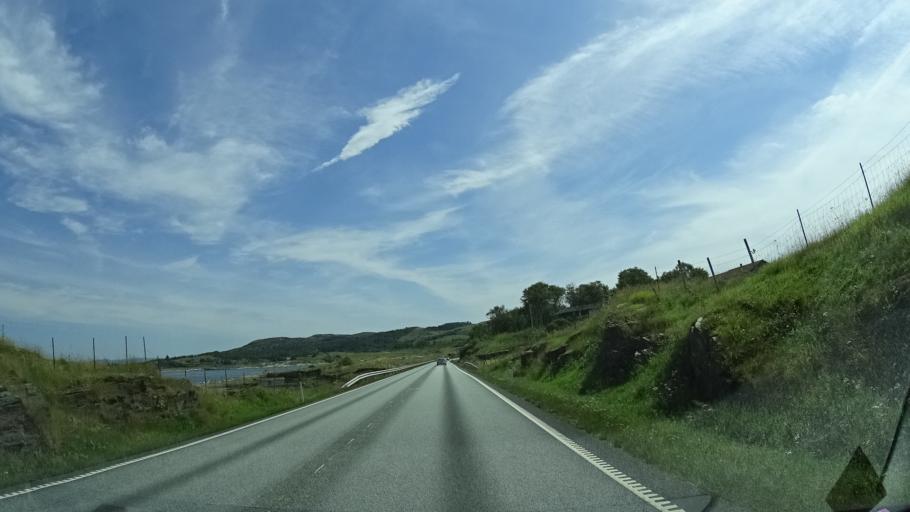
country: NO
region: Rogaland
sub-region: Rennesoy
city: Vikevag
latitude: 59.1208
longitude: 5.6872
